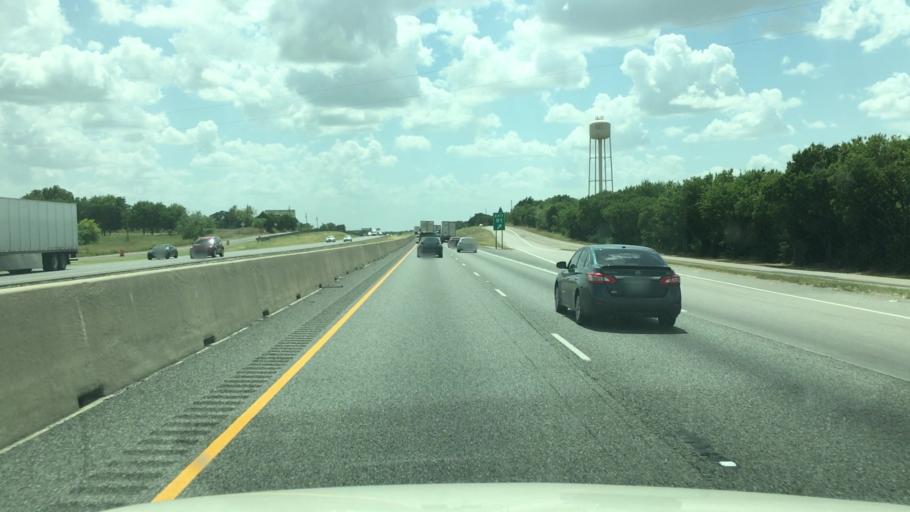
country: US
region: Texas
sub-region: Hunt County
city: Caddo Mills
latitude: 32.9959
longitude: -96.2455
